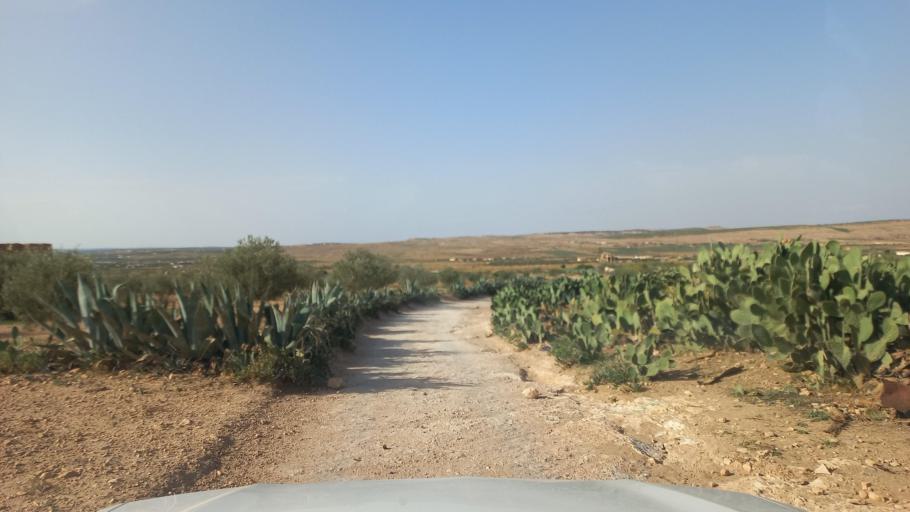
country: TN
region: Al Qasrayn
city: Kasserine
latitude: 35.3363
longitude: 8.8450
